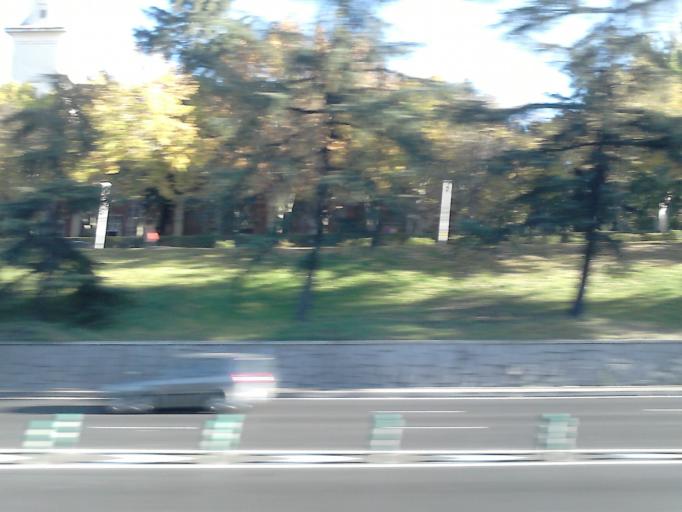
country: ES
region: Madrid
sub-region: Provincia de Madrid
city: Moncloa-Aravaca
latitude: 40.4384
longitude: -3.7246
